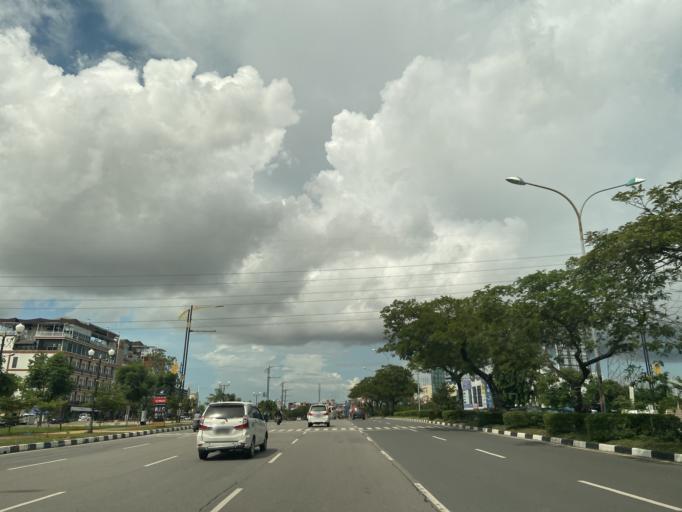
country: SG
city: Singapore
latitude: 1.1248
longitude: 104.0253
